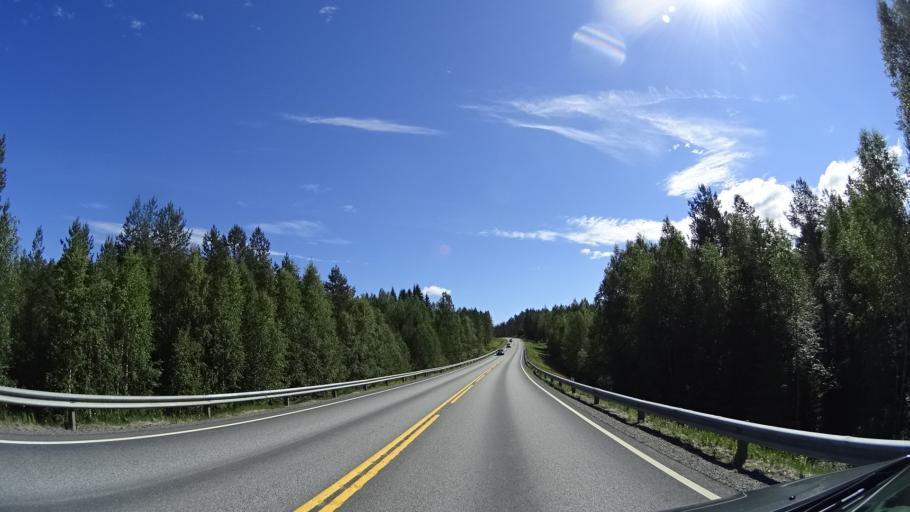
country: FI
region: Pirkanmaa
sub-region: Luoteis-Pirkanmaa
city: Kihnioe
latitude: 62.2451
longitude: 23.4061
